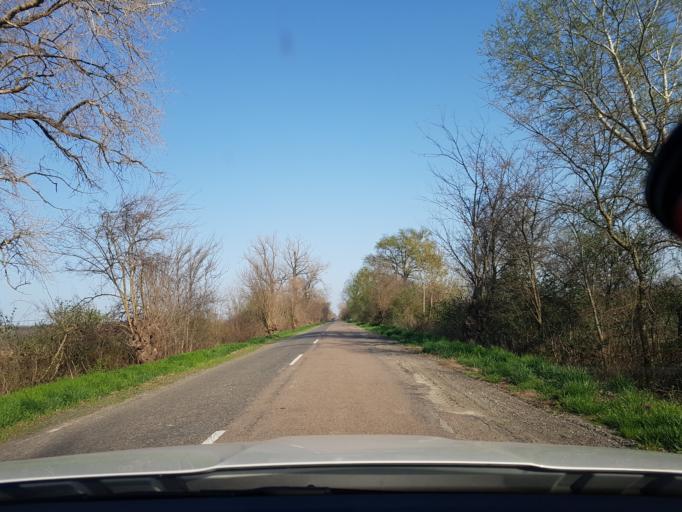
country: HU
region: Tolna
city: Ocseny
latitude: 46.3365
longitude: 18.7906
